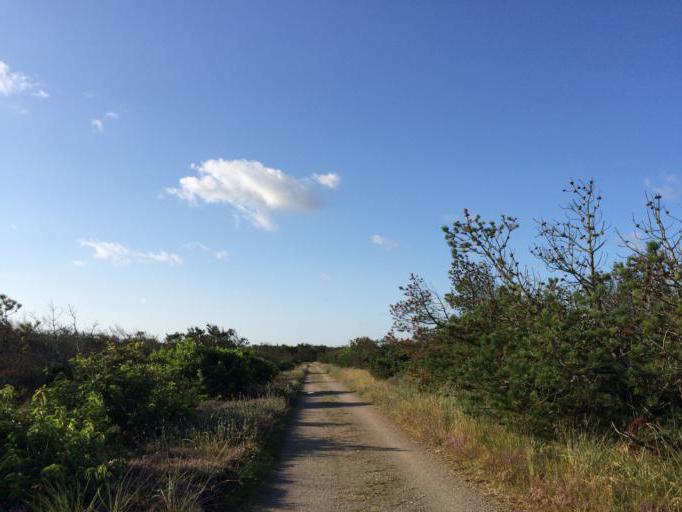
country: DK
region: Central Jutland
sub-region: Holstebro Kommune
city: Ulfborg
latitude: 56.3134
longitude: 8.1324
